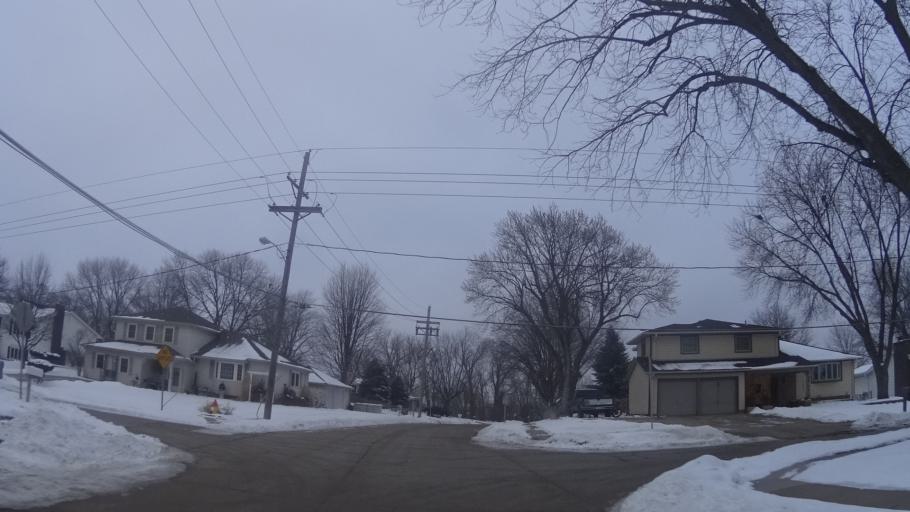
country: US
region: Nebraska
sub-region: Sarpy County
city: Offutt Air Force Base
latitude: 41.1494
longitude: -95.9250
